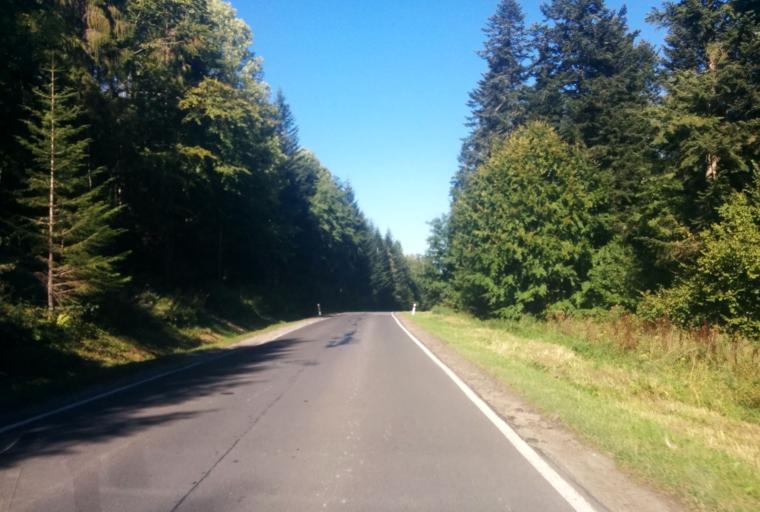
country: PL
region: Subcarpathian Voivodeship
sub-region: Powiat bieszczadzki
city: Czarna
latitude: 49.2935
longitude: 22.6713
